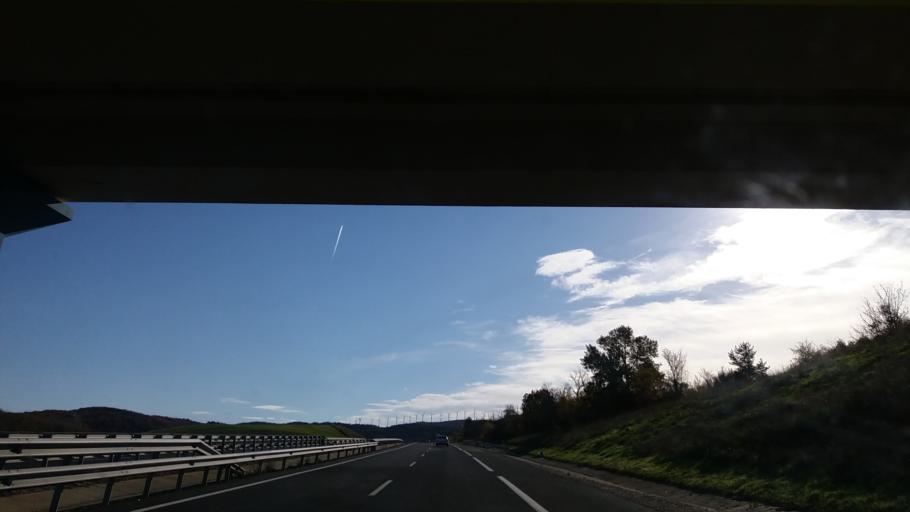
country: ES
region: Navarre
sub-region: Provincia de Navarra
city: Leache
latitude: 42.6666
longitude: -1.4340
